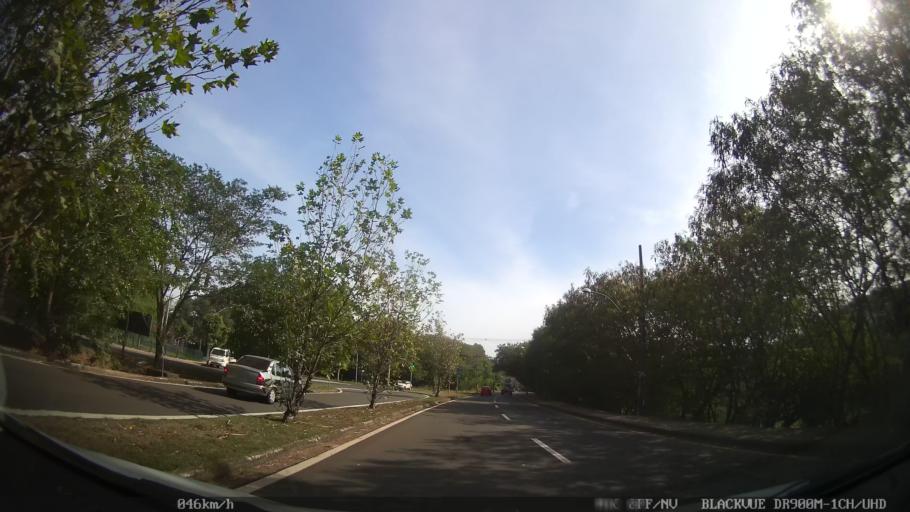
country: BR
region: Sao Paulo
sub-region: Piracicaba
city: Piracicaba
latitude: -22.7233
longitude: -47.6715
